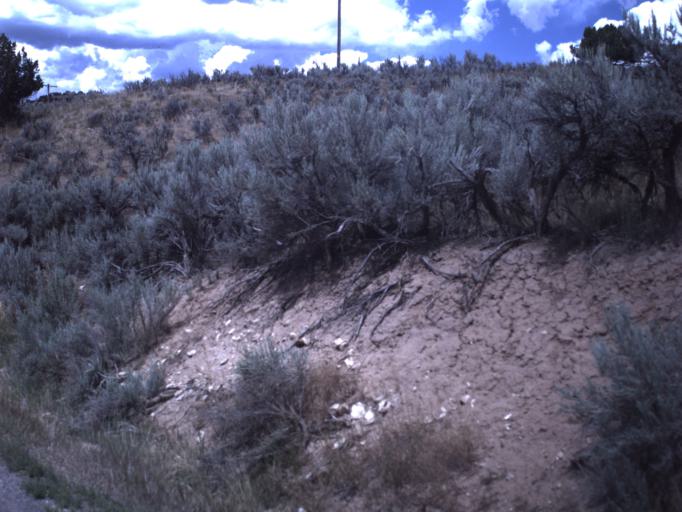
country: US
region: Utah
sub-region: Summit County
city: Oakley
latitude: 40.7561
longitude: -111.3732
